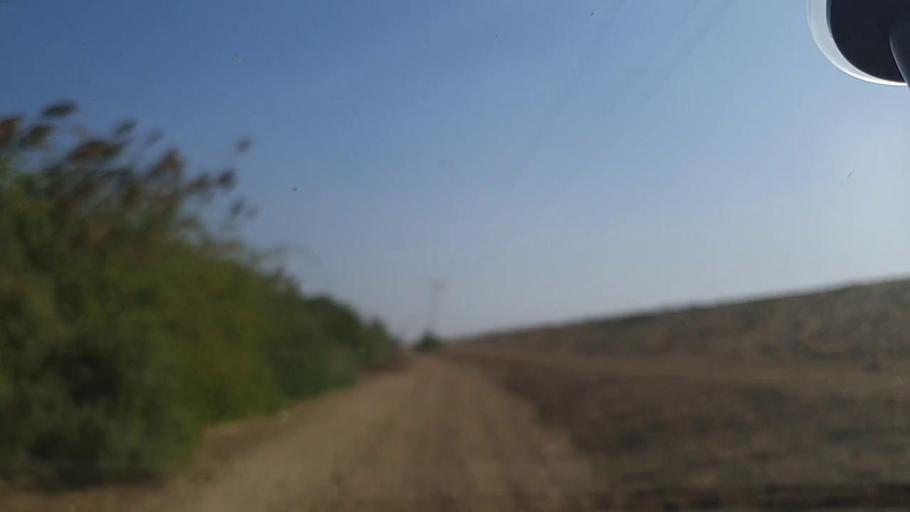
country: PK
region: Sindh
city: Chuhar Jamali
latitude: 24.4622
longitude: 67.8894
